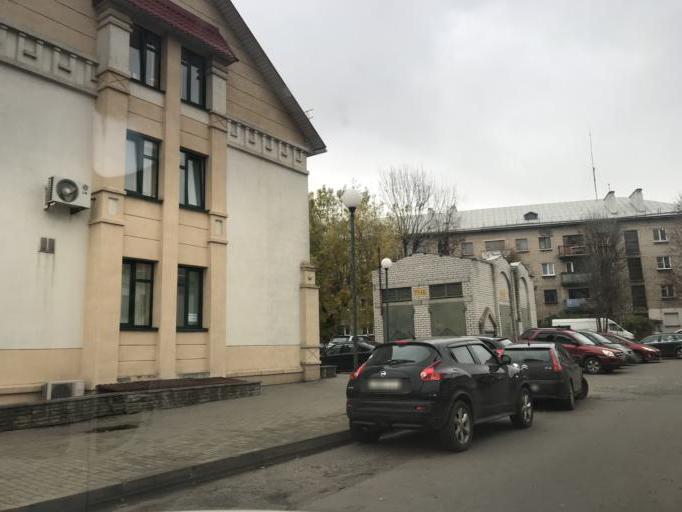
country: BY
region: Mogilev
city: Mahilyow
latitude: 53.8955
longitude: 30.3348
